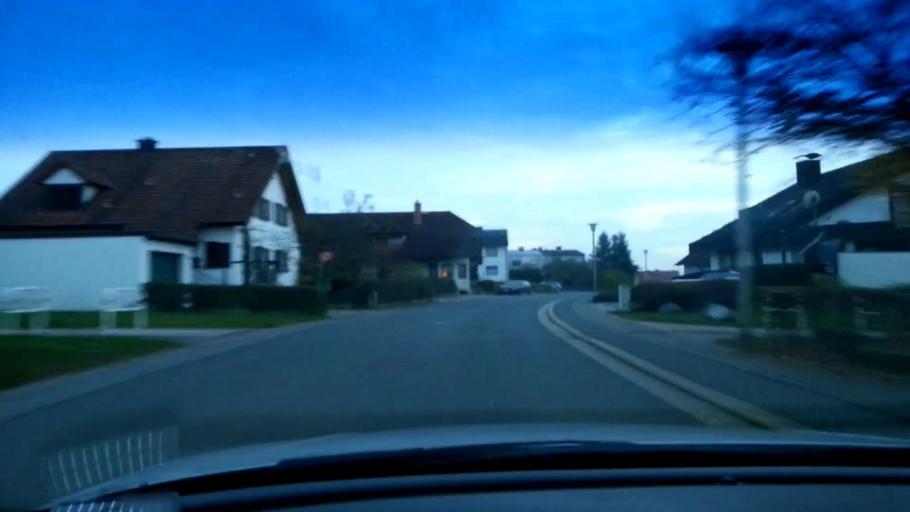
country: DE
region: Bavaria
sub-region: Upper Franconia
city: Breitengussbach
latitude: 49.9743
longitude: 10.8967
